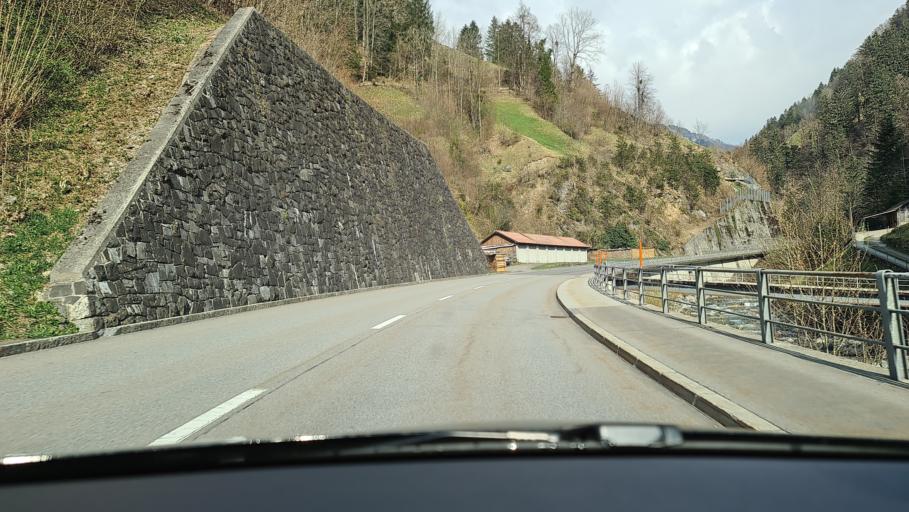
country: CH
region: Uri
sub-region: Uri
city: Burglen
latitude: 46.8776
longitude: 8.6855
